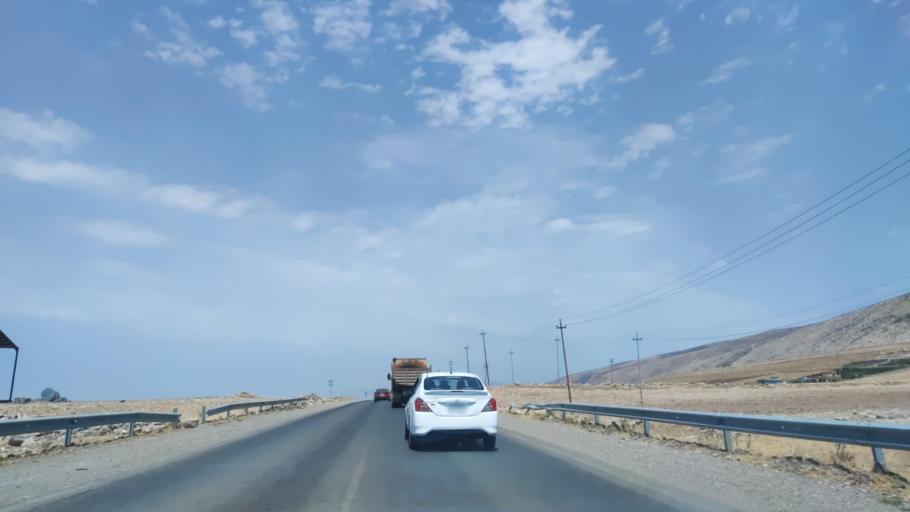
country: IQ
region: Arbil
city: Shaqlawah
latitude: 36.5169
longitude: 44.3712
